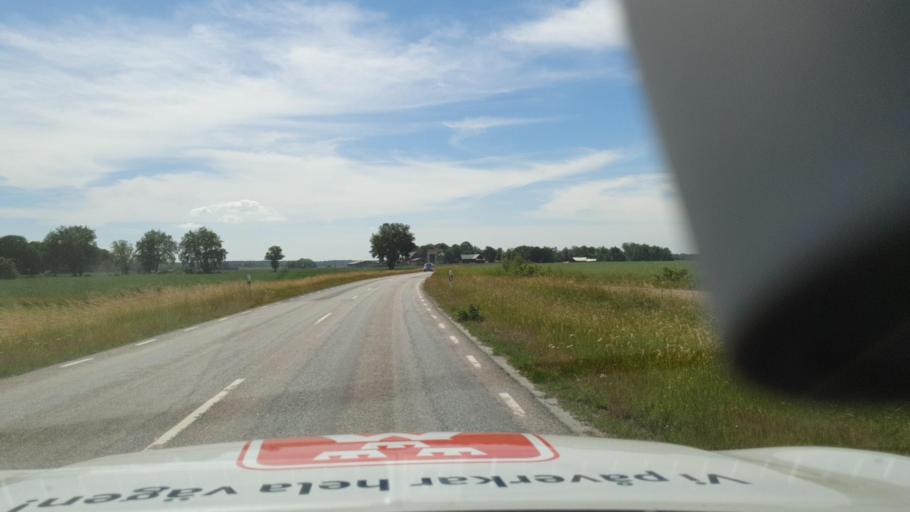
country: SE
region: Vaestra Goetaland
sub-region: Lidkopings Kommun
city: Lidkoping
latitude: 58.5130
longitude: 13.0533
